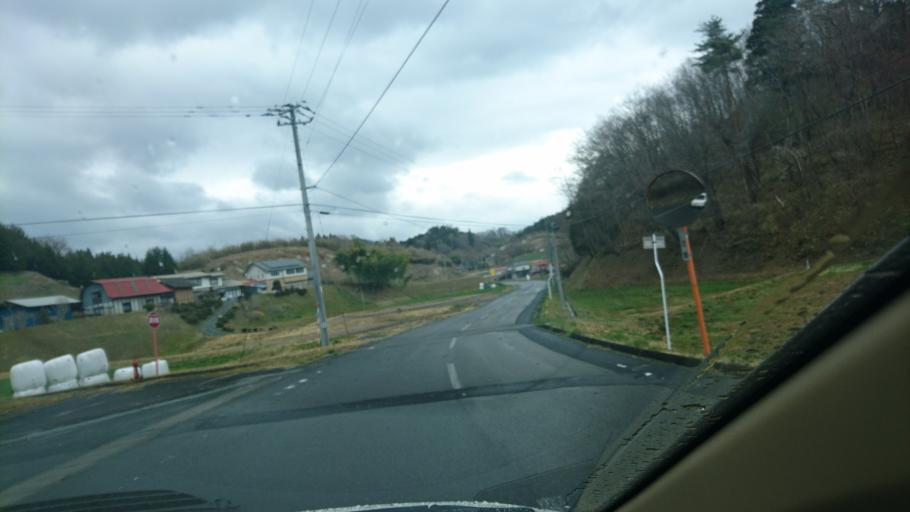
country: JP
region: Iwate
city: Ichinoseki
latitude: 38.9424
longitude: 141.3184
